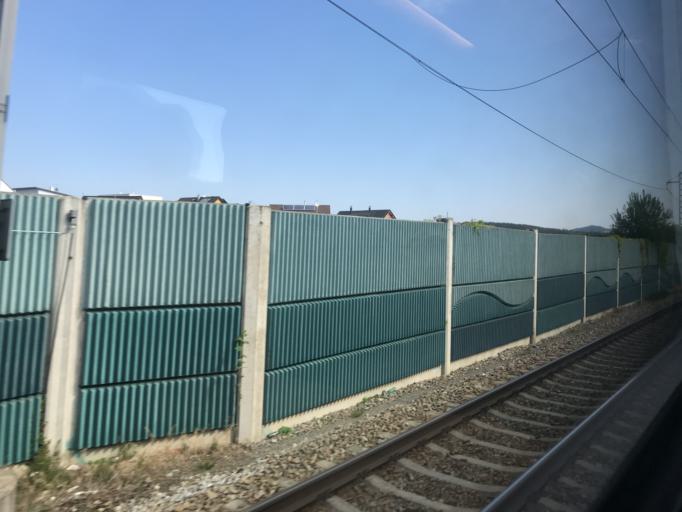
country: CZ
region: Central Bohemia
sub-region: Okres Benesov
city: Benesov
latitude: 49.7913
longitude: 14.6953
